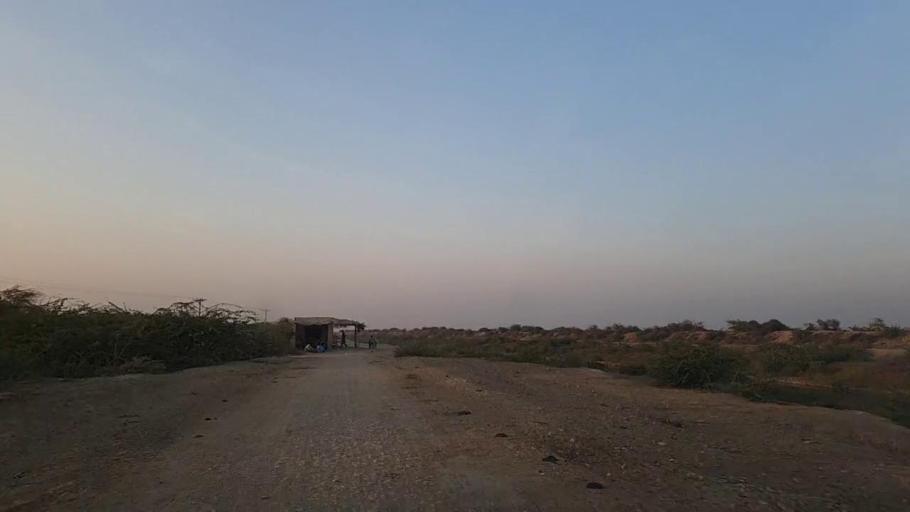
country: PK
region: Sindh
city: Naukot
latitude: 24.9526
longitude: 69.4280
